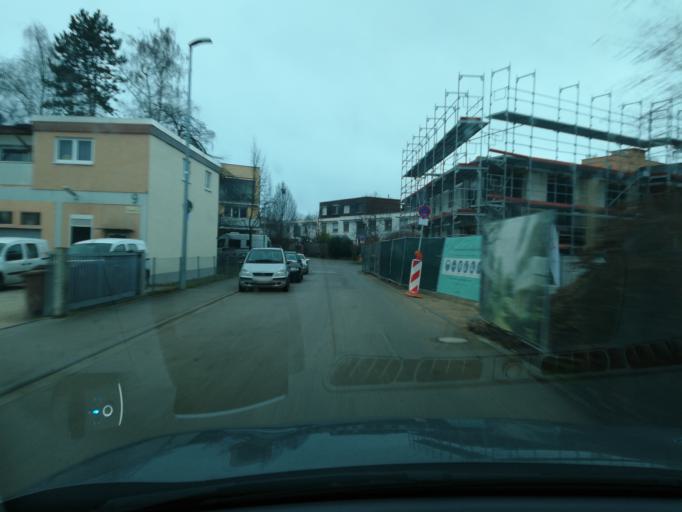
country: DE
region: Baden-Wuerttemberg
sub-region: Regierungsbezirk Stuttgart
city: Schorndorf
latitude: 48.8075
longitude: 9.5209
